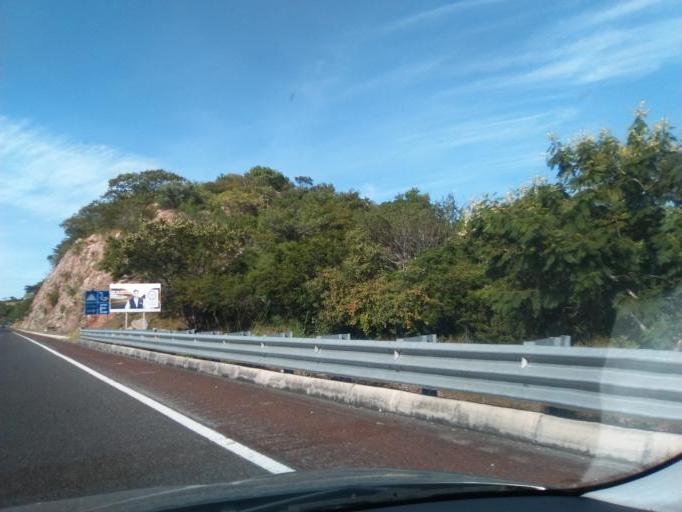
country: MX
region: Guerrero
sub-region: Huitzuco de los Figueroa
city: Ciudad de Huitzuco
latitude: 18.1958
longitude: -99.2064
